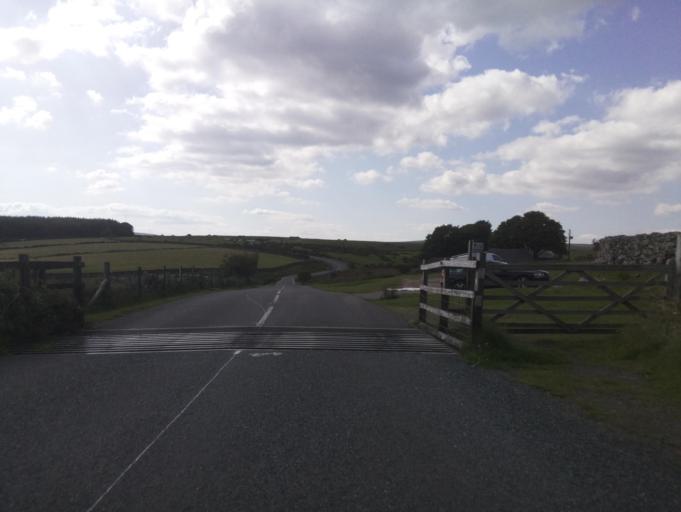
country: GB
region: England
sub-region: Devon
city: South Brent
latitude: 50.5550
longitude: -3.9127
